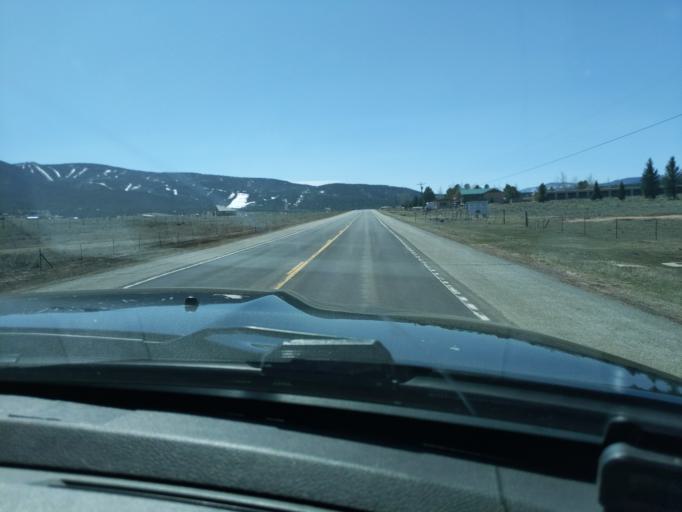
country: US
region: New Mexico
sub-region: Colfax County
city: Angel Fire
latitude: 36.4146
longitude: -105.2943
